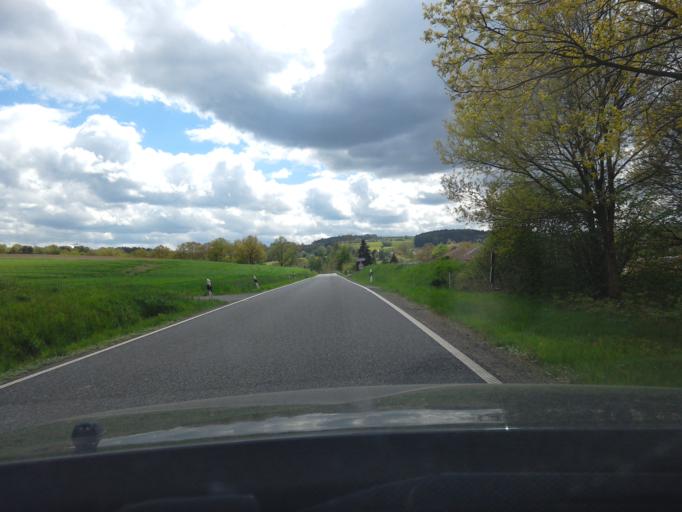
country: DE
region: Bavaria
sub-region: Regierungsbezirk Unterfranken
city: Aura im Sinngrund
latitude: 50.2142
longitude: 9.4890
